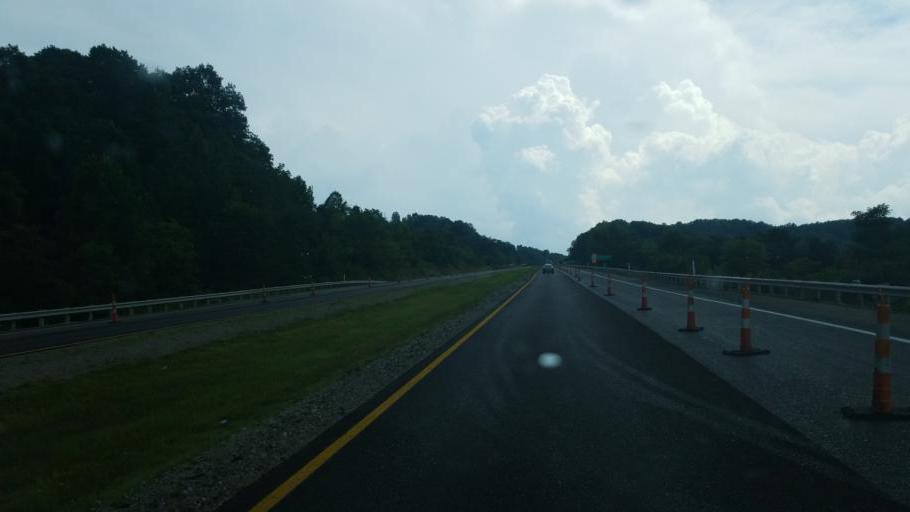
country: US
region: West Virginia
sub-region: Kanawha County
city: Alum Creek
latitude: 38.2550
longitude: -81.8369
